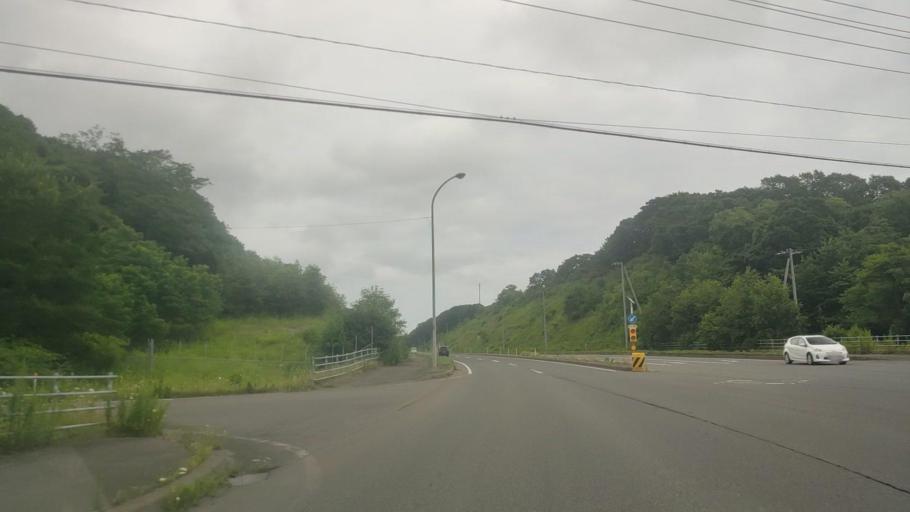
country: JP
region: Hokkaido
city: Shiraoi
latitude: 42.4562
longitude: 141.1906
